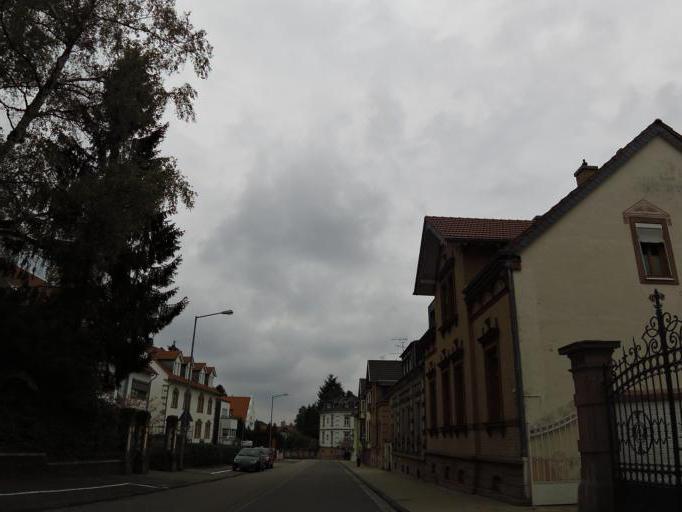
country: DE
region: Saarland
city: Sankt Ingbert
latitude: 49.2721
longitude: 7.1110
